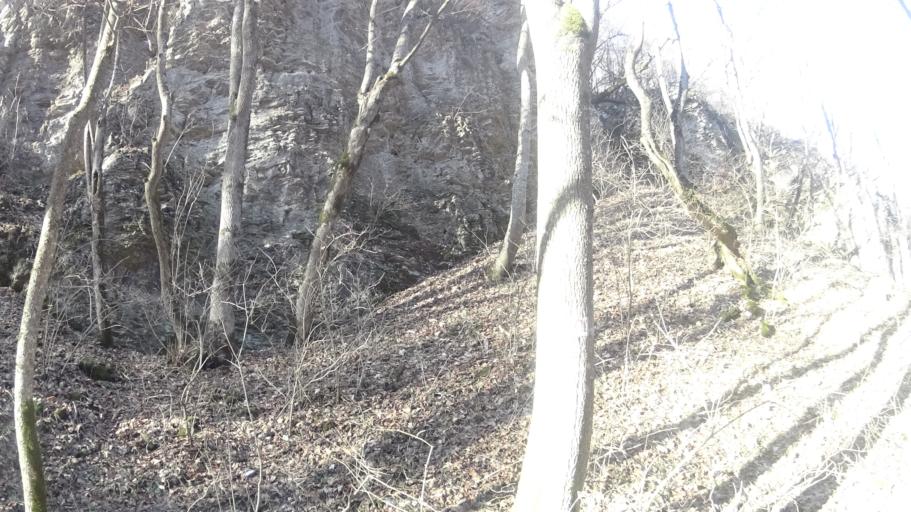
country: HU
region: Borsod-Abauj-Zemplen
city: Bogacs
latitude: 48.0009
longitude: 20.5221
